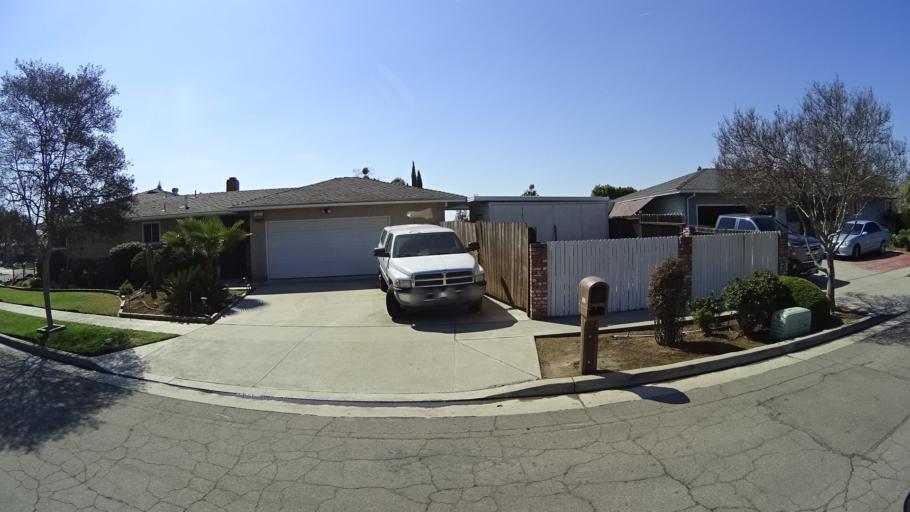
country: US
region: California
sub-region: Fresno County
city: Clovis
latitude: 36.8313
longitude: -119.7374
